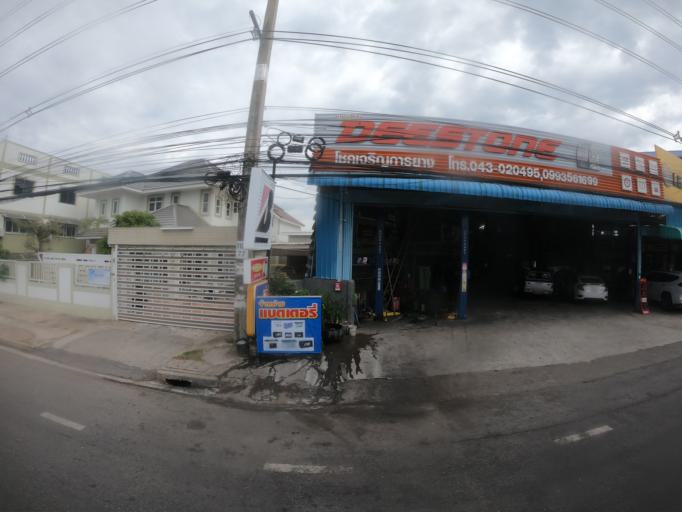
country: TH
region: Maha Sarakham
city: Maha Sarakham
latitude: 16.1929
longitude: 103.2942
